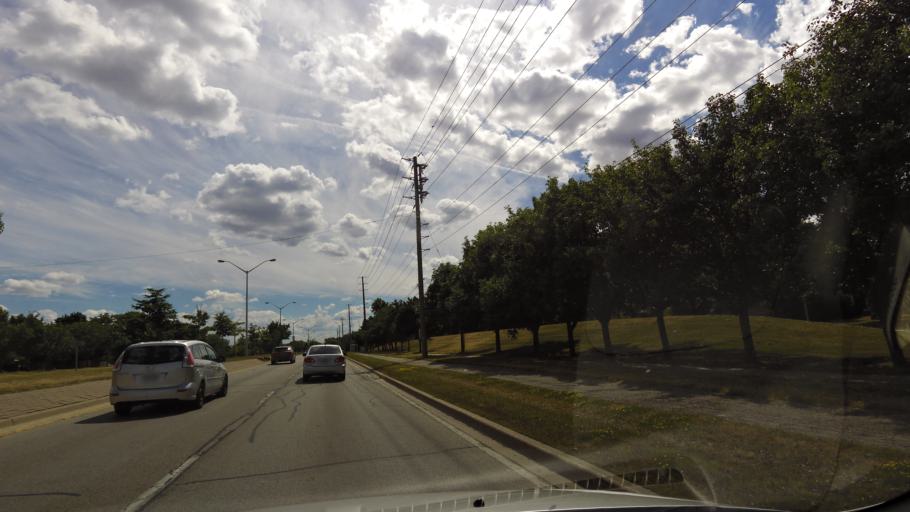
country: CA
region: Ontario
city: Oakville
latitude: 43.4658
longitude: -79.7124
